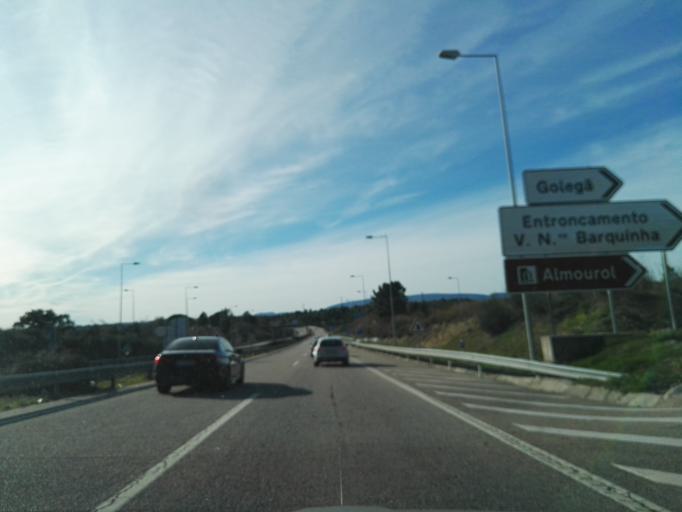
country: PT
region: Santarem
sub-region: Entroncamento
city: Entroncamento
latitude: 39.4889
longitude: -8.4482
